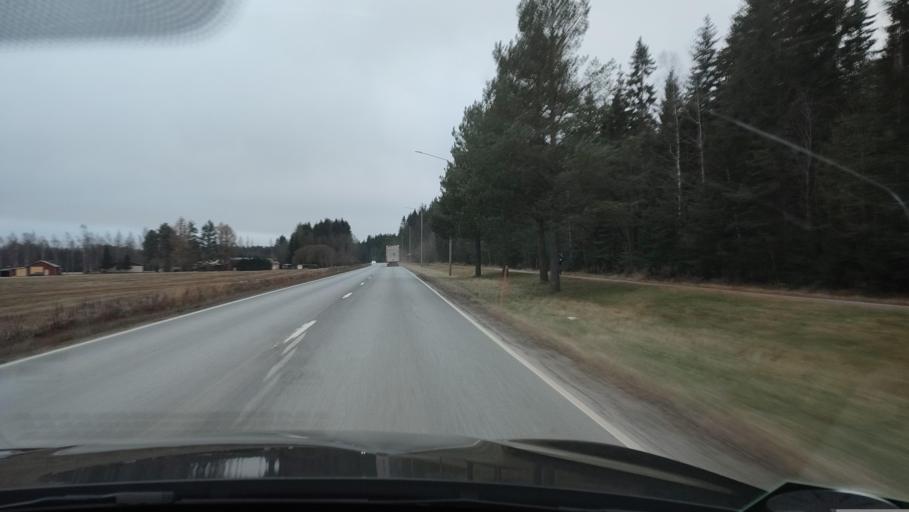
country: FI
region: Southern Ostrobothnia
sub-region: Suupohja
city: Kauhajoki
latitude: 62.4062
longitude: 22.1635
